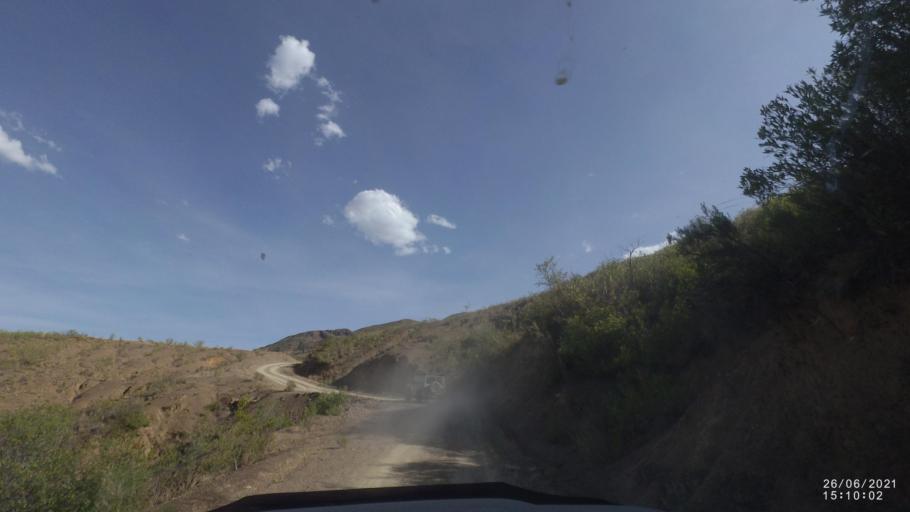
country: BO
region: Cochabamba
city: Mizque
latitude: -17.9526
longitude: -65.6410
